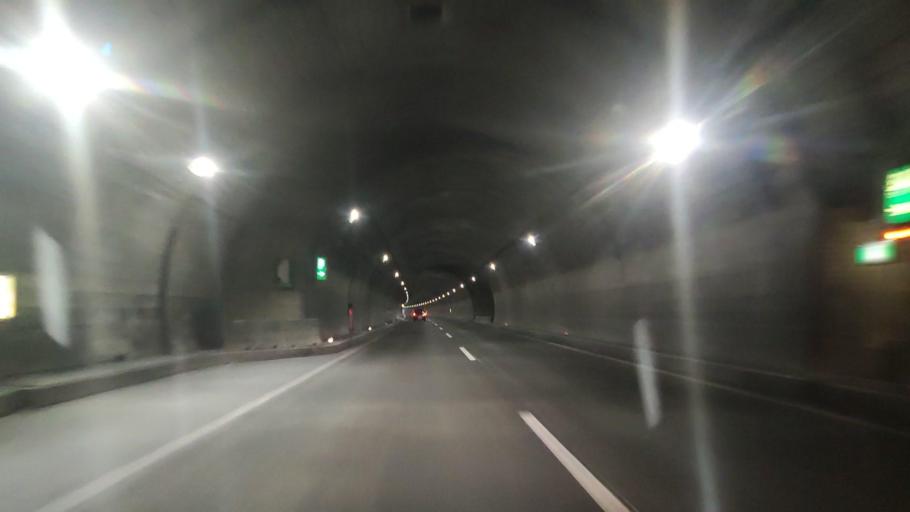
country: JP
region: Oita
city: Beppu
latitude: 33.2733
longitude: 131.3426
